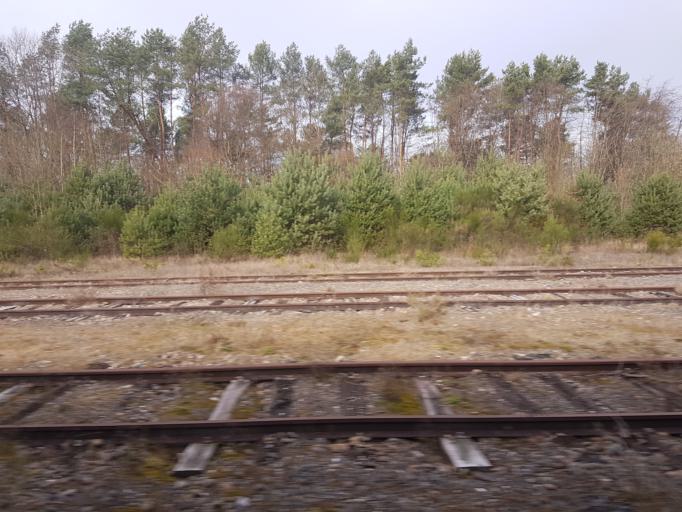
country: FR
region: Franche-Comte
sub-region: Departement de la Haute-Saone
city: Aillevillers-et-Lyaumont
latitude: 47.9127
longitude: 6.3353
